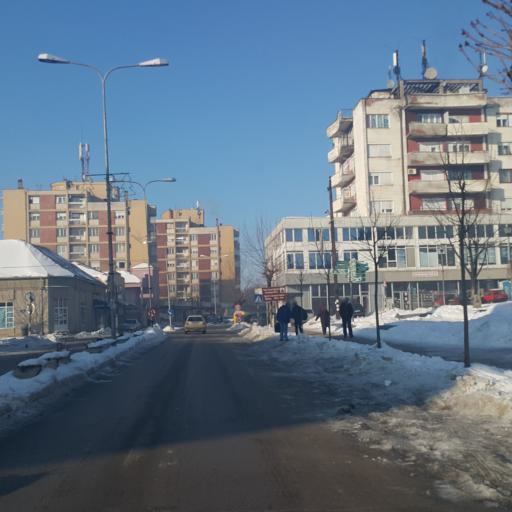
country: RS
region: Central Serbia
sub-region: Toplicki Okrug
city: Blace
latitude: 43.2957
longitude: 21.2870
